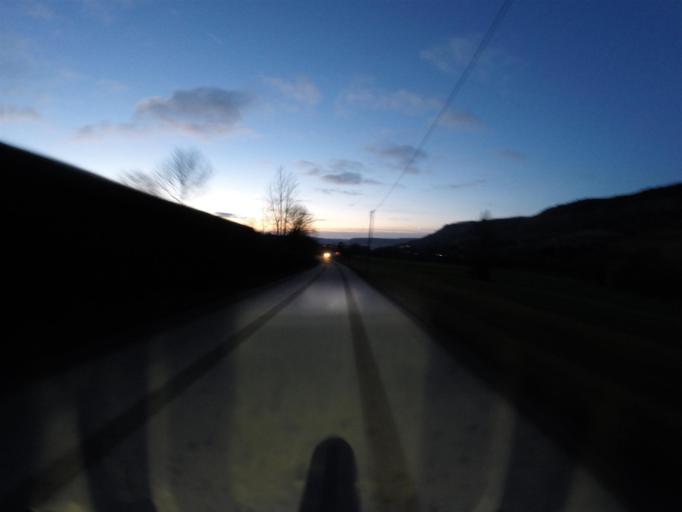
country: DE
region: Thuringia
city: Grosslobichau
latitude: 50.9308
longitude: 11.6470
